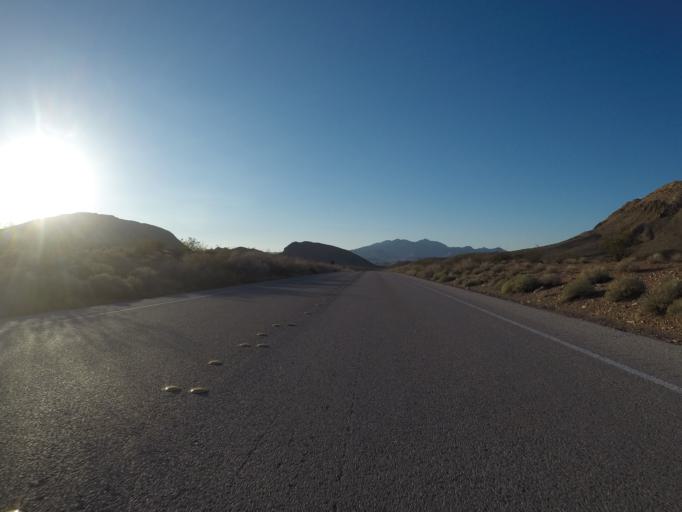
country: US
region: Nevada
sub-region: Clark County
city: Moapa Valley
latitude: 36.2429
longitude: -114.5342
